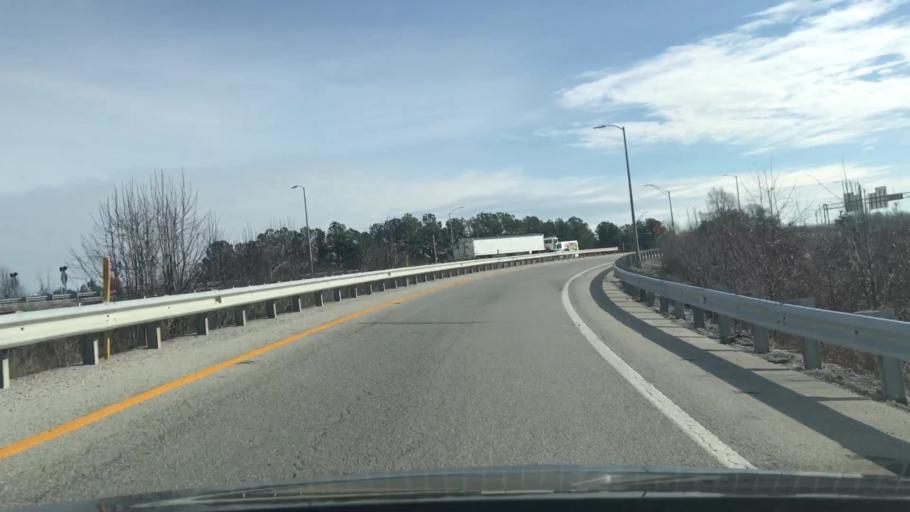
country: US
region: Kentucky
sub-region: Daviess County
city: Owensboro
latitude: 37.7394
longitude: -87.0724
